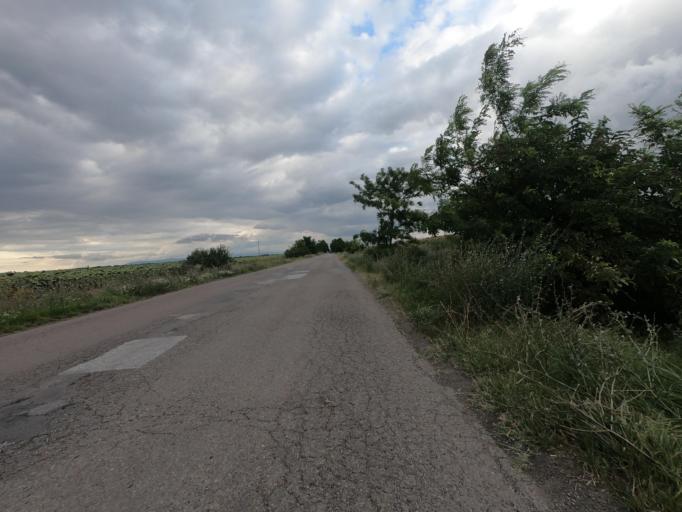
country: HU
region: Heves
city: Poroszlo
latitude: 47.6794
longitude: 20.6523
